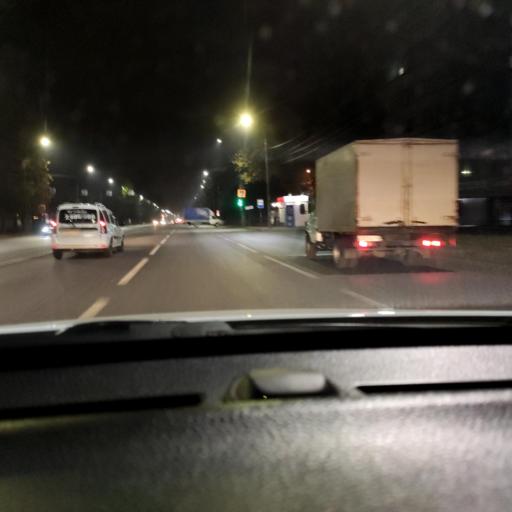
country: RU
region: Voronezj
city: Voronezh
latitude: 51.6797
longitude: 39.1759
